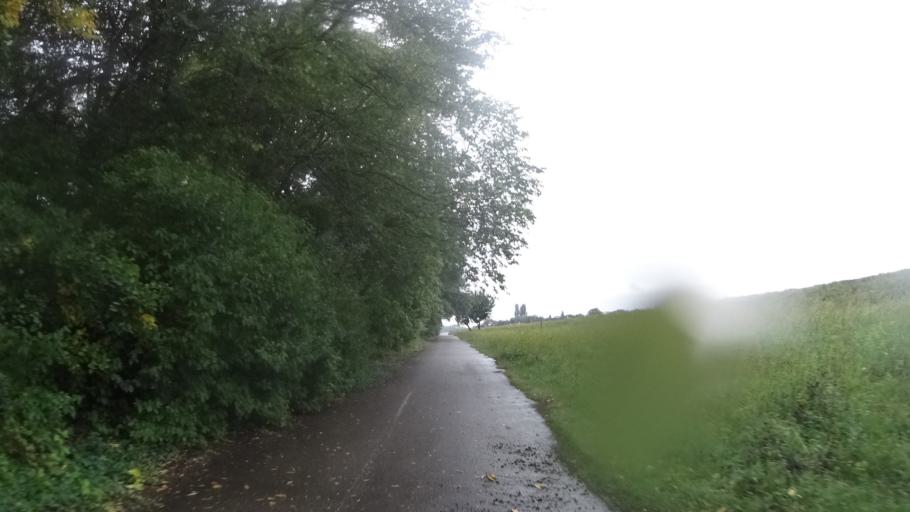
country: HU
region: Komarom-Esztergom
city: Labatlan
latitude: 47.7557
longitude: 18.4950
